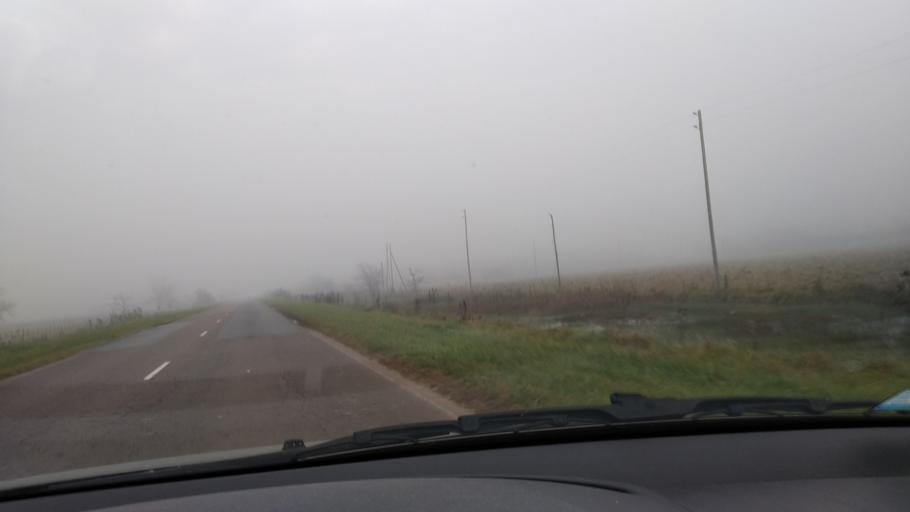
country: AR
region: Buenos Aires
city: San Miguel del Monte
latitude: -35.3067
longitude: -58.5957
